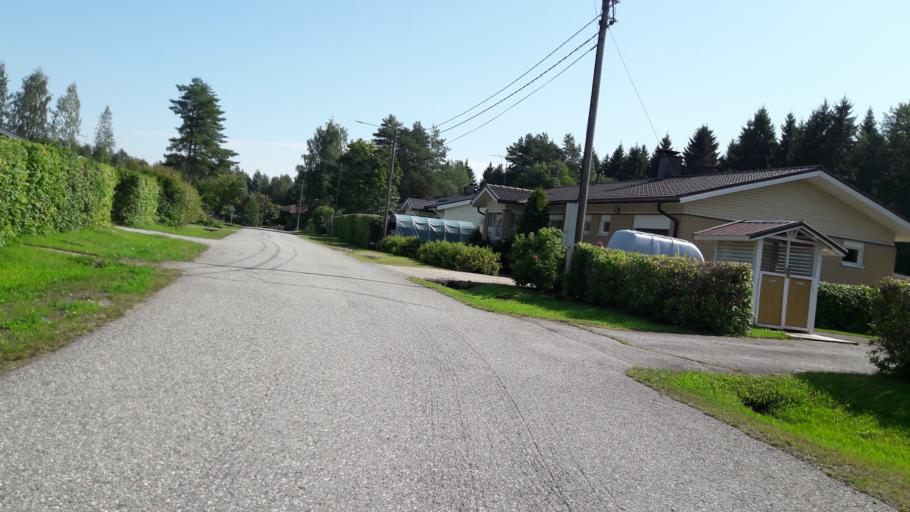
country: FI
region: North Karelia
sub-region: Joensuu
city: Joensuu
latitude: 62.5352
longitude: 29.8329
